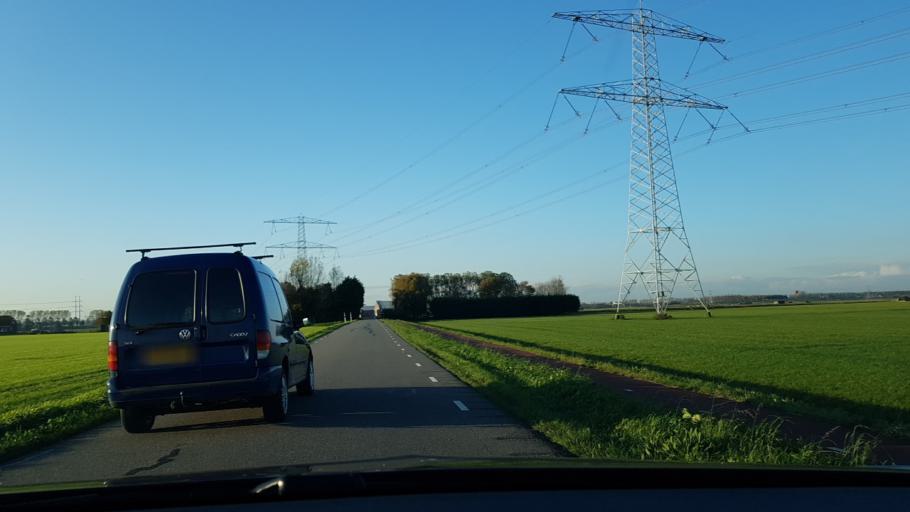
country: NL
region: North Holland
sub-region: Gemeente Beverwijk
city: Beverwijk
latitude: 52.4668
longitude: 4.6980
